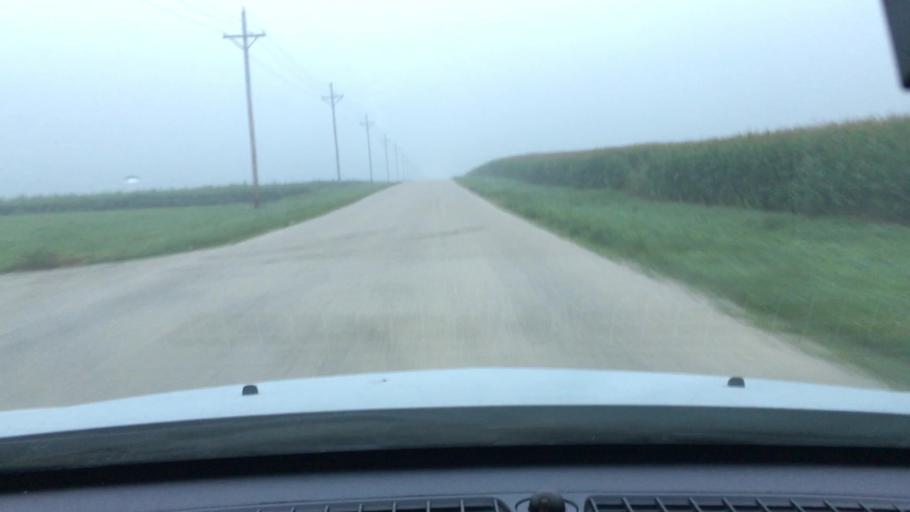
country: US
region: Illinois
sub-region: Ogle County
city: Rochelle
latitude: 41.8987
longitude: -88.9740
